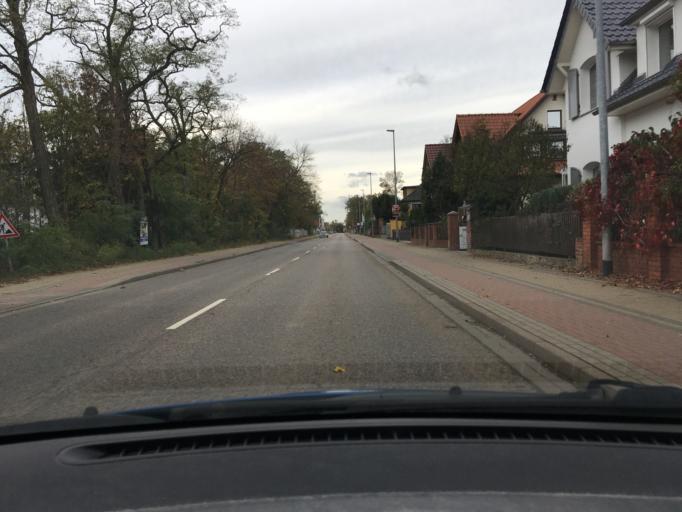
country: DE
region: Saxony-Anhalt
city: Biederitz
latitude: 52.1361
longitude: 11.7435
